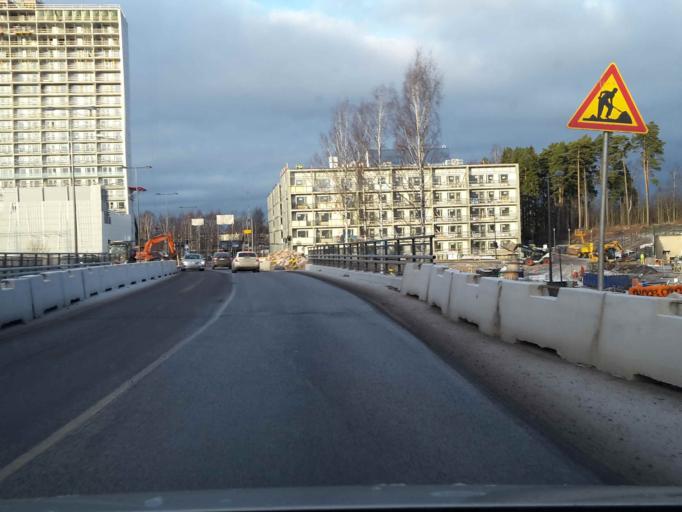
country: FI
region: Uusimaa
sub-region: Helsinki
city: Koukkuniemi
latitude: 60.1686
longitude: 24.7668
